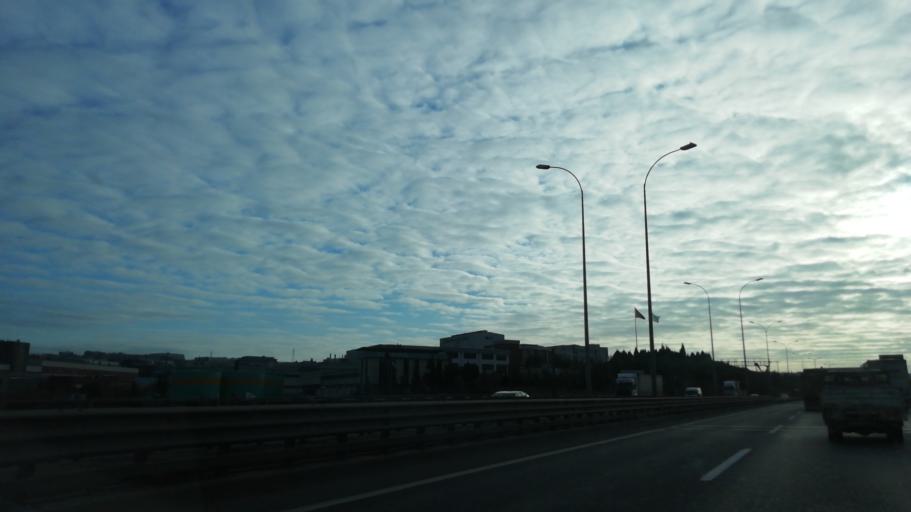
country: TR
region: Kocaeli
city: Balcik
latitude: 40.8766
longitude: 29.3876
